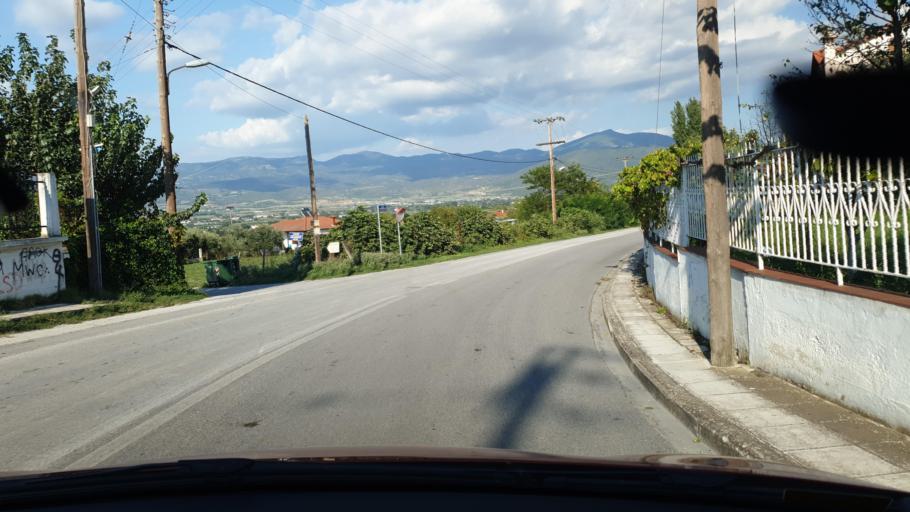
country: GR
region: Central Macedonia
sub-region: Nomos Thessalonikis
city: Souroti
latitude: 40.4742
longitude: 23.0925
